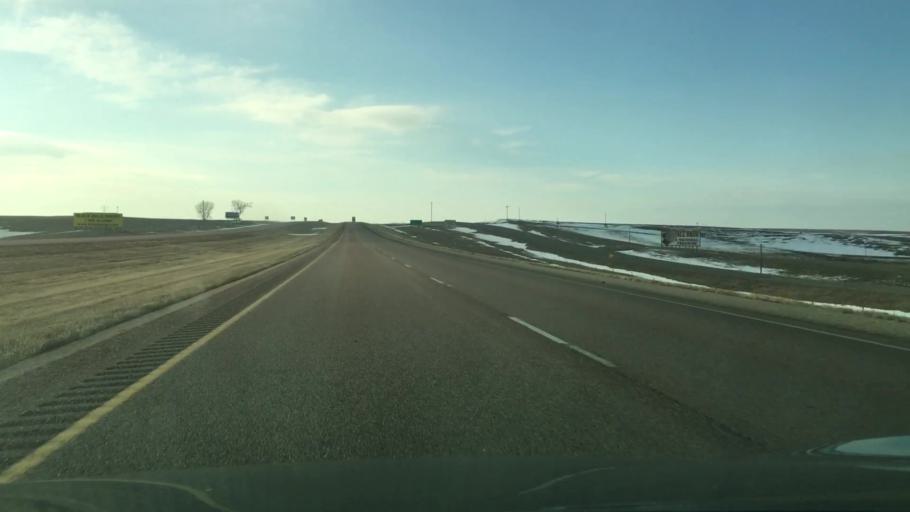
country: US
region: South Dakota
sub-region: Lyman County
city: Kennebec
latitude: 43.8975
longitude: -99.8791
